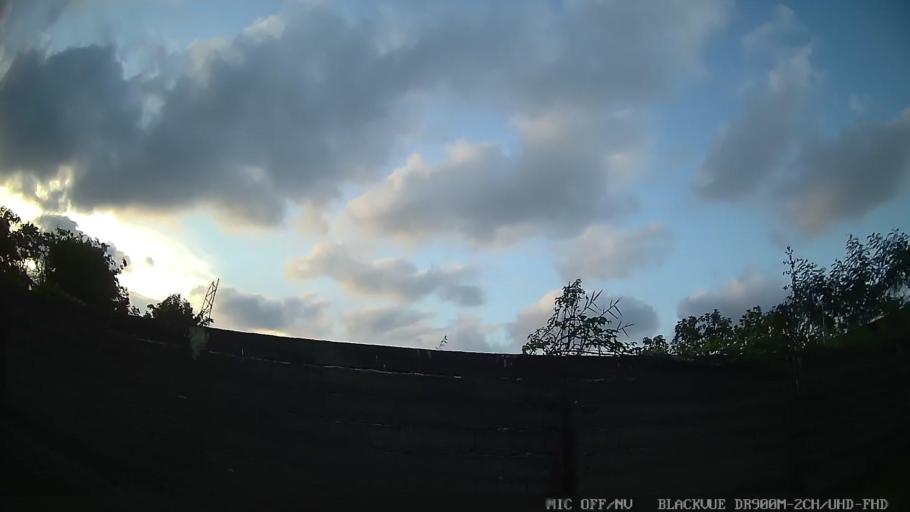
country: BR
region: Sao Paulo
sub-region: Peruibe
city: Peruibe
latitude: -24.3241
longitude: -47.0086
